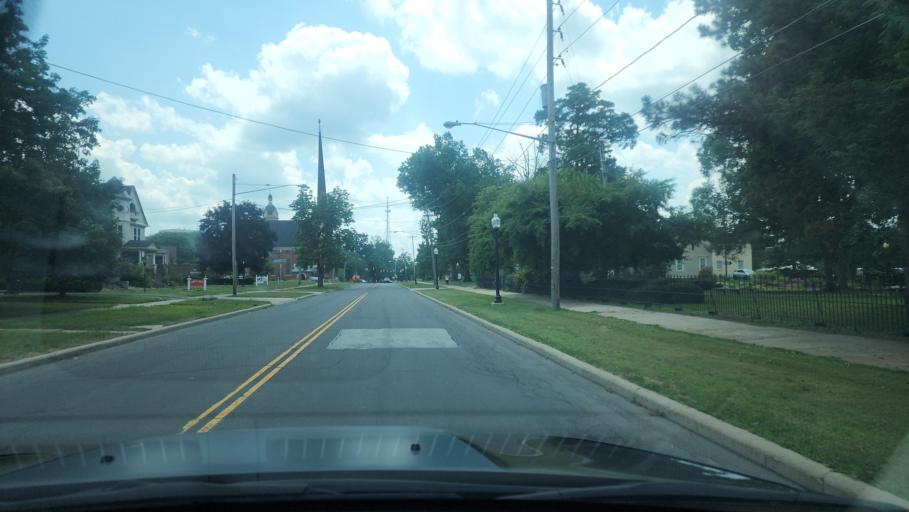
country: US
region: Ohio
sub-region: Trumbull County
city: Warren
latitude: 41.2394
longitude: -80.8226
